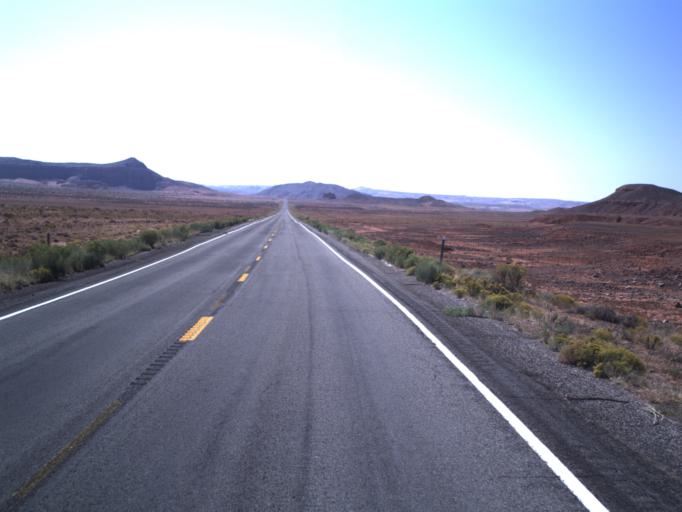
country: US
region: Utah
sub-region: San Juan County
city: Blanding
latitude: 37.0114
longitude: -109.6124
